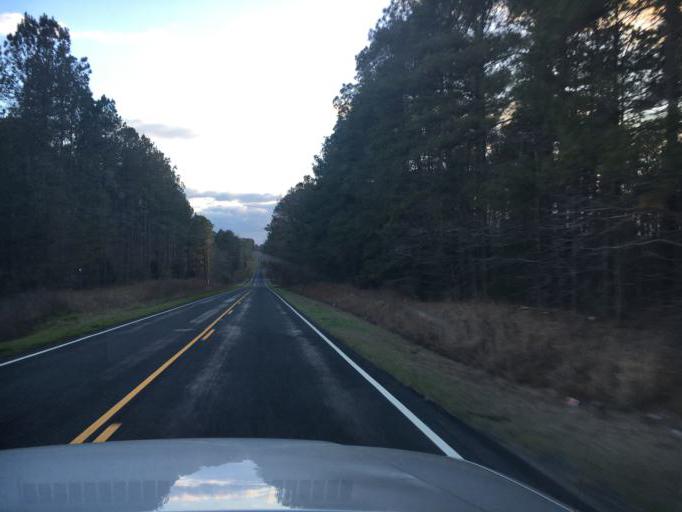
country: US
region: South Carolina
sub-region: Greenwood County
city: Greenwood
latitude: 34.0639
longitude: -82.2306
